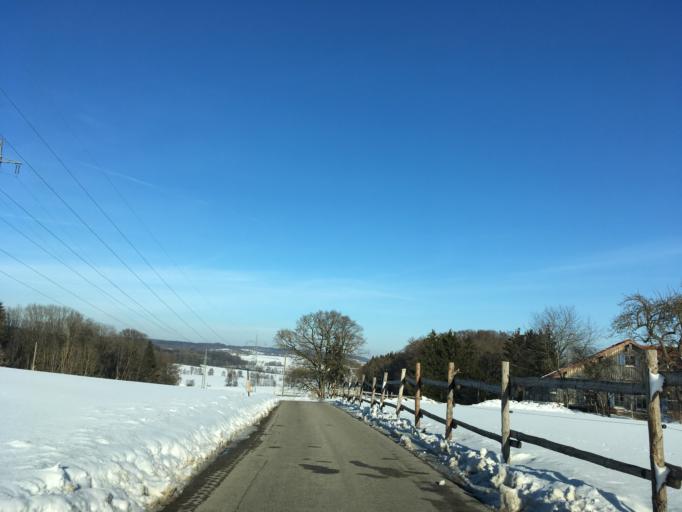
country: DE
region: Bavaria
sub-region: Upper Bavaria
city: Steinhoring
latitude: 48.0950
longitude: 12.0034
